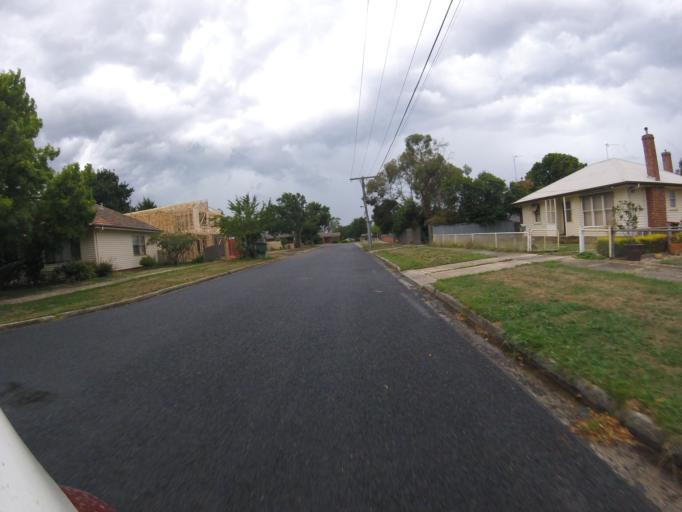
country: AU
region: Victoria
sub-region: Ballarat North
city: Newington
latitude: -37.5566
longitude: 143.8085
